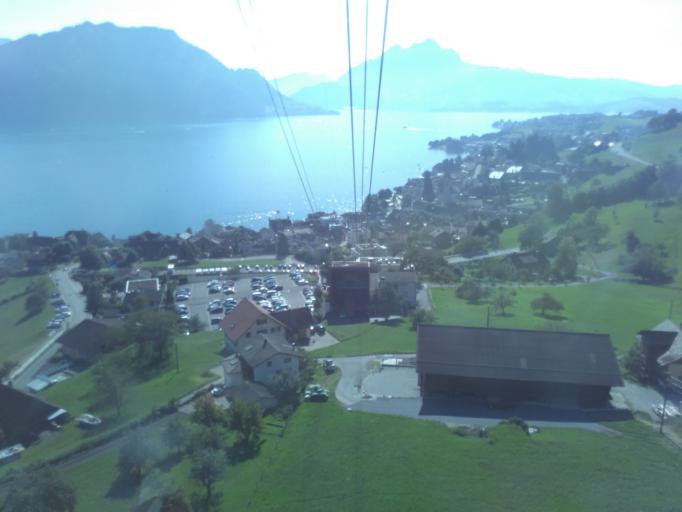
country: CH
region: Lucerne
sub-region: Lucerne-Land District
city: Weggis
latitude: 47.0349
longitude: 8.4428
